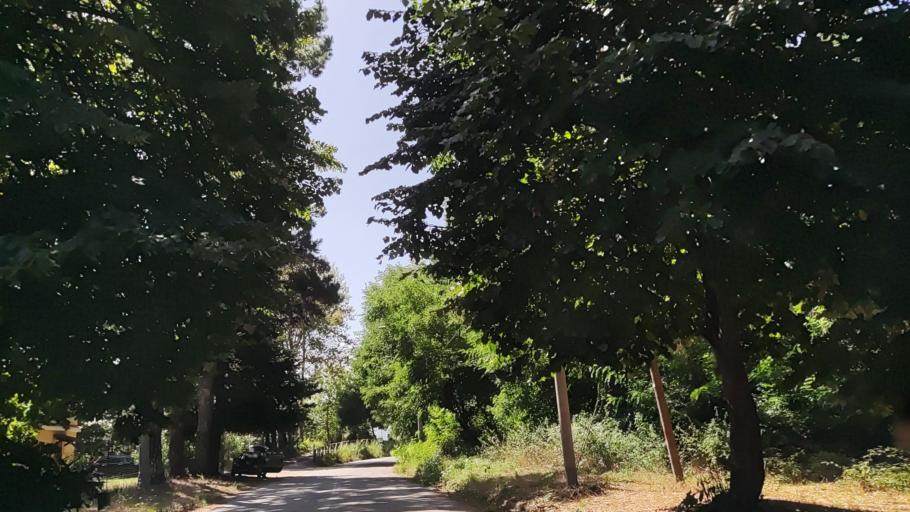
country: IT
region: Calabria
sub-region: Provincia di Reggio Calabria
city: Seminara
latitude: 38.3390
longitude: 15.8454
